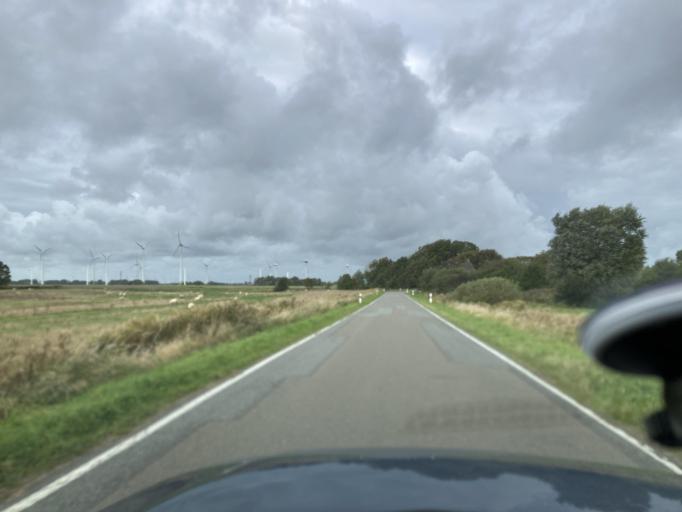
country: DE
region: Schleswig-Holstein
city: Wesselburener Deichhausen
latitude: 54.1727
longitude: 8.9318
